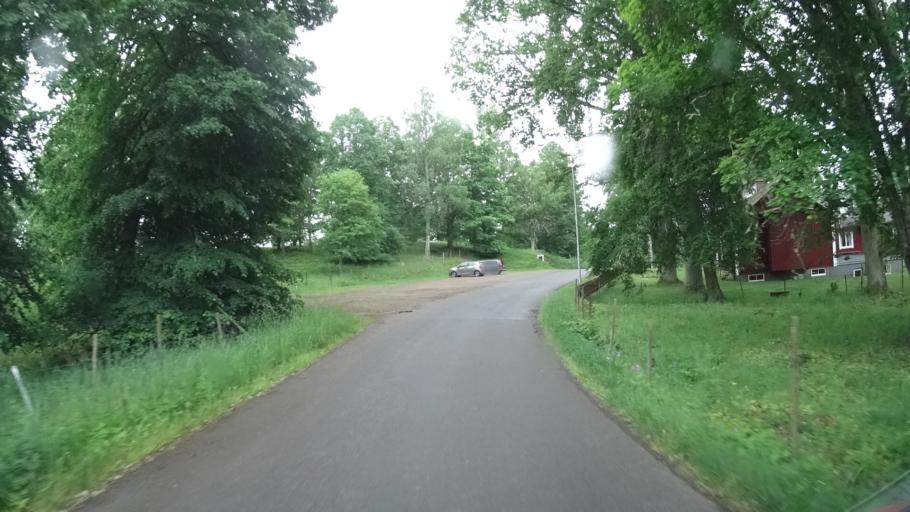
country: SE
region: Joenkoeping
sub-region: Eksjo Kommun
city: Mariannelund
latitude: 57.6796
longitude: 15.5812
